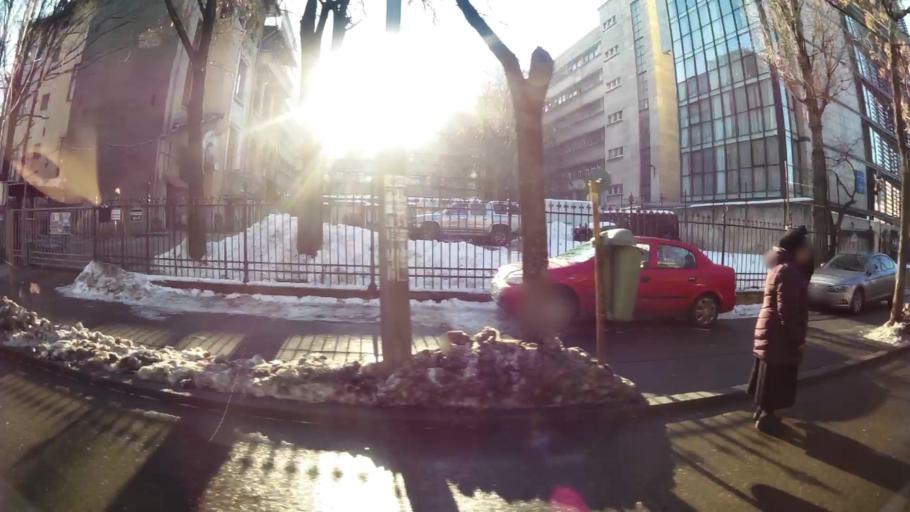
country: RO
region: Bucuresti
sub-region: Municipiul Bucuresti
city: Bucuresti
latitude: 44.4456
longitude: 26.0918
